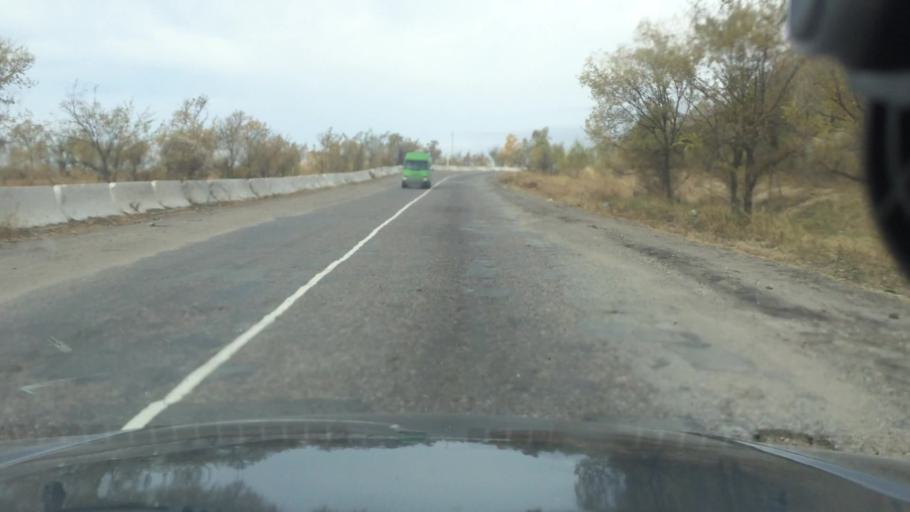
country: KG
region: Ysyk-Koel
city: Karakol
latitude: 42.5968
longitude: 78.3783
